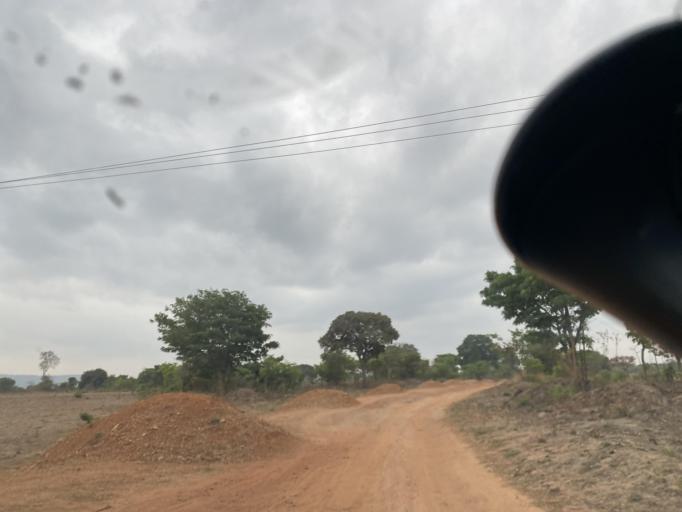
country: ZM
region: Lusaka
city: Chongwe
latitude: -15.2280
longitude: 28.7280
